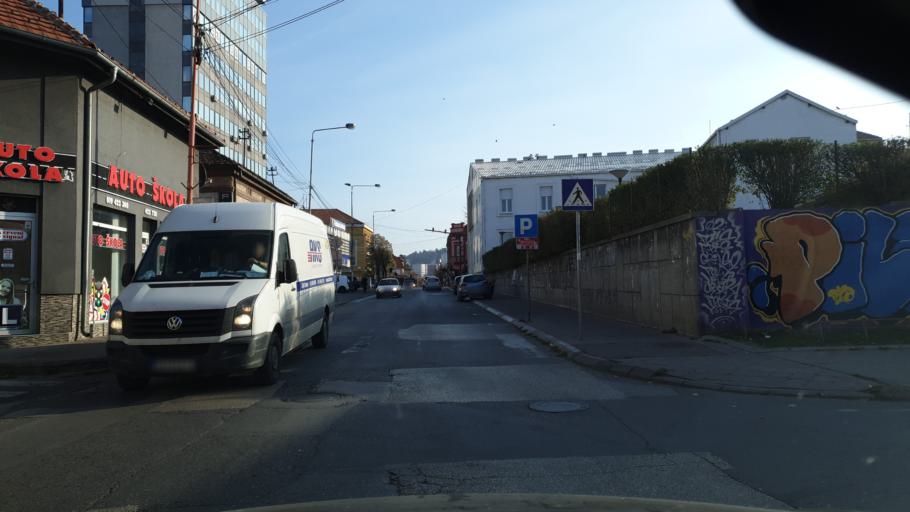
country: RS
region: Central Serbia
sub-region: Zajecarski Okrug
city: Zajecar
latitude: 43.9043
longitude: 22.2795
